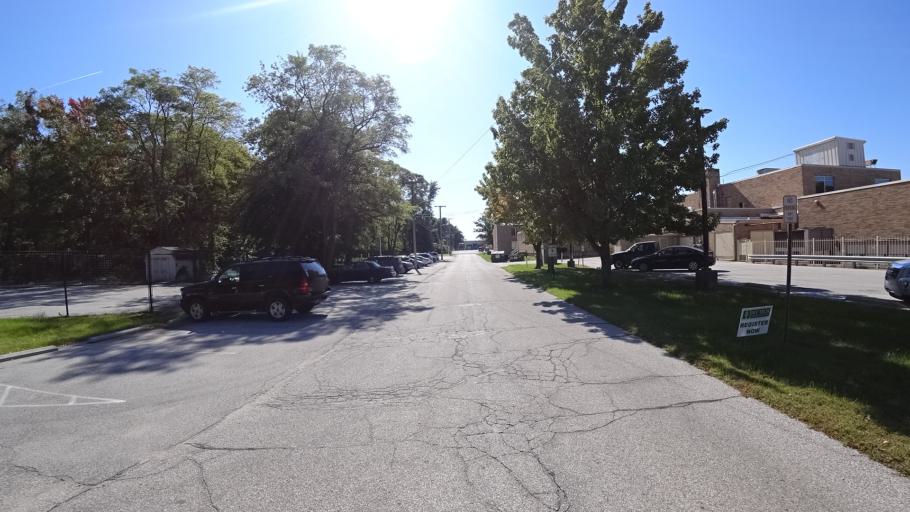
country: US
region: Indiana
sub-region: LaPorte County
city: Michigan City
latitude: 41.6863
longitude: -86.8927
